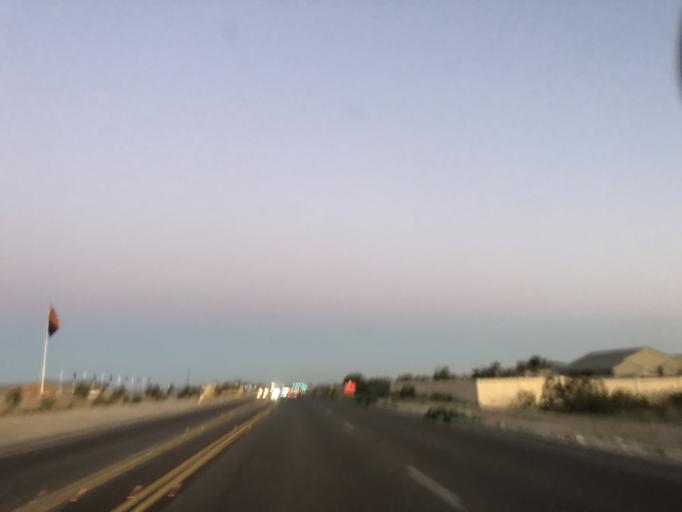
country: US
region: Arizona
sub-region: Maricopa County
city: Citrus Park
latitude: 33.4937
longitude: -112.4875
